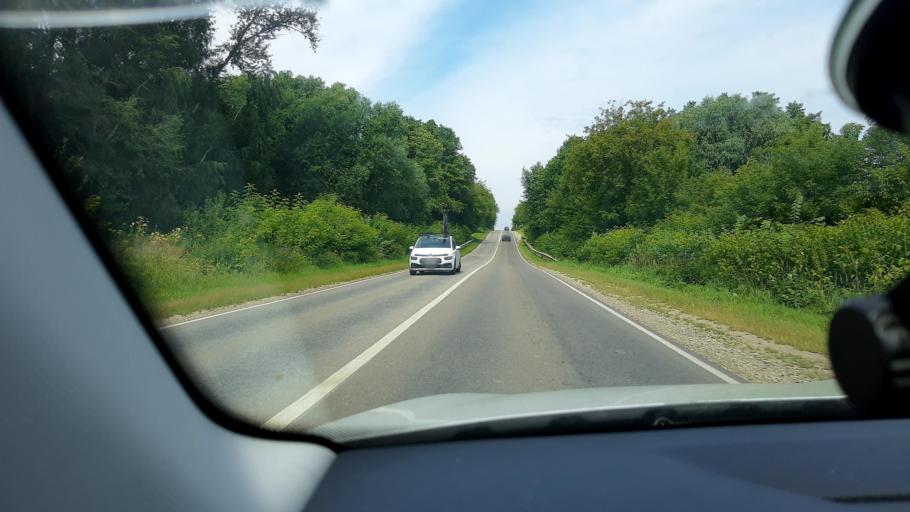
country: RU
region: Tula
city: Zaokskiy
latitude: 54.7814
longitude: 37.4345
